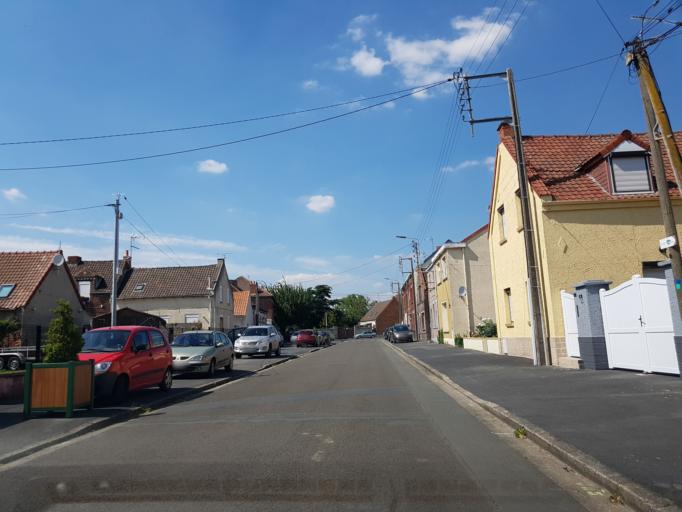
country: FR
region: Nord-Pas-de-Calais
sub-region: Departement du Nord
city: Roeulx
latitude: 50.3041
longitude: 3.3327
